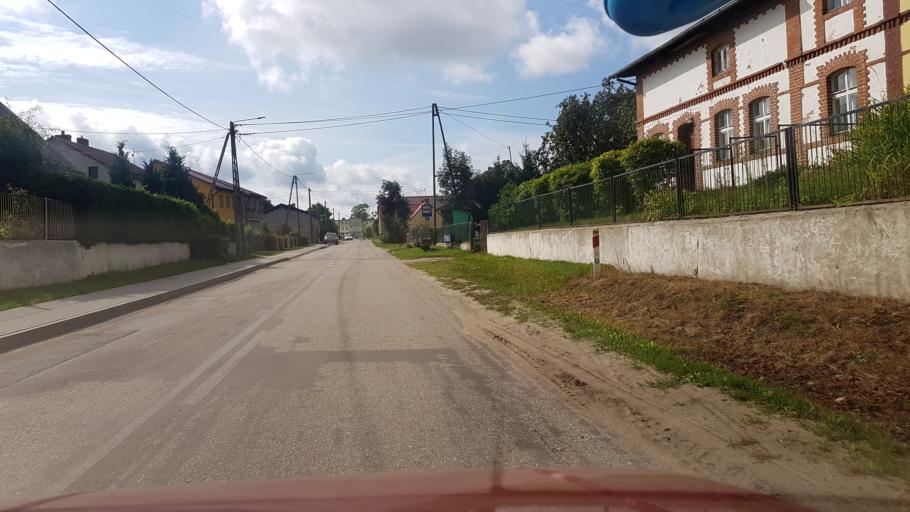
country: PL
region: Pomeranian Voivodeship
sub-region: Powiat bytowski
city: Miastko
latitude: 54.0850
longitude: 16.8539
